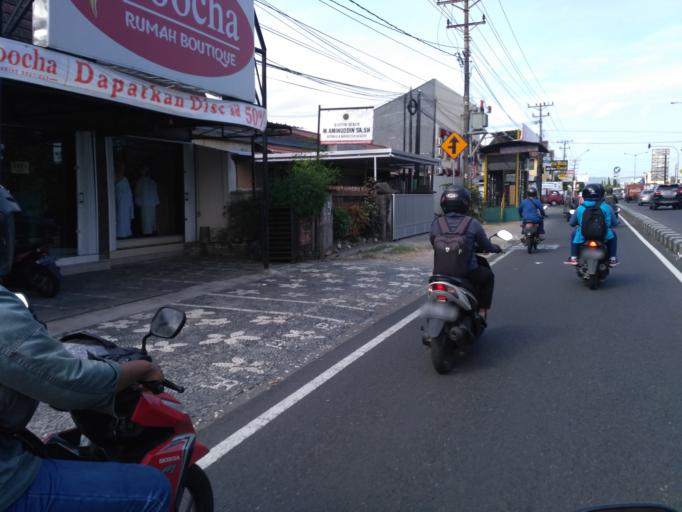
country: ID
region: Daerah Istimewa Yogyakarta
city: Depok
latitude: -7.7643
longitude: 110.4233
